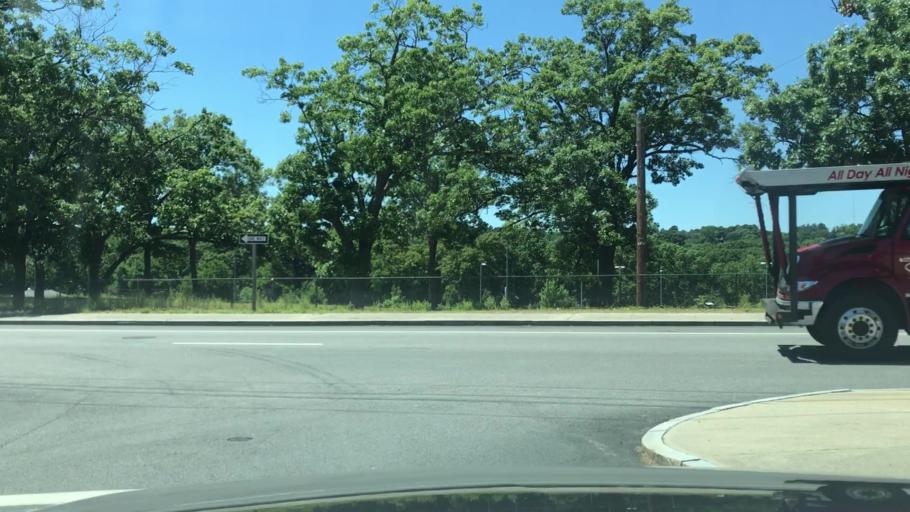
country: US
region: Rhode Island
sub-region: Providence County
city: Pawtucket
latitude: 41.8637
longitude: -71.3752
